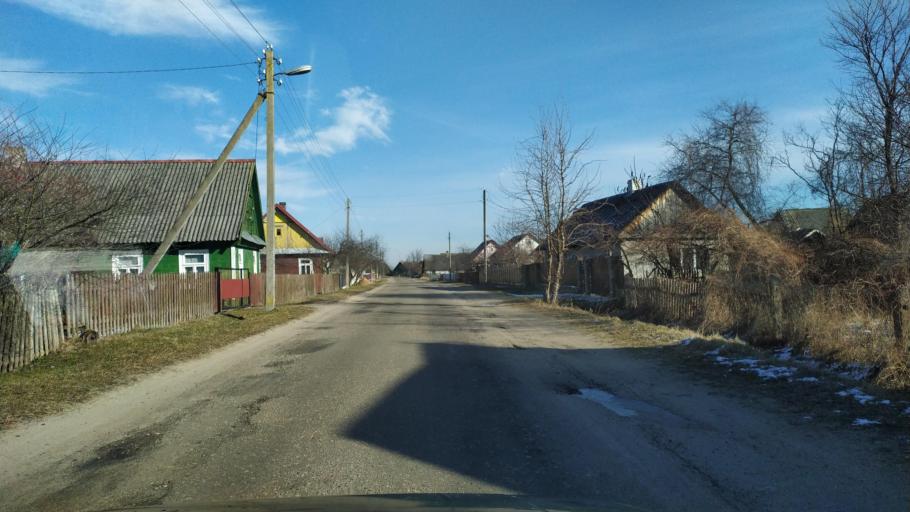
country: BY
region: Brest
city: Kamyanyets
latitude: 52.4036
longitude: 23.7954
